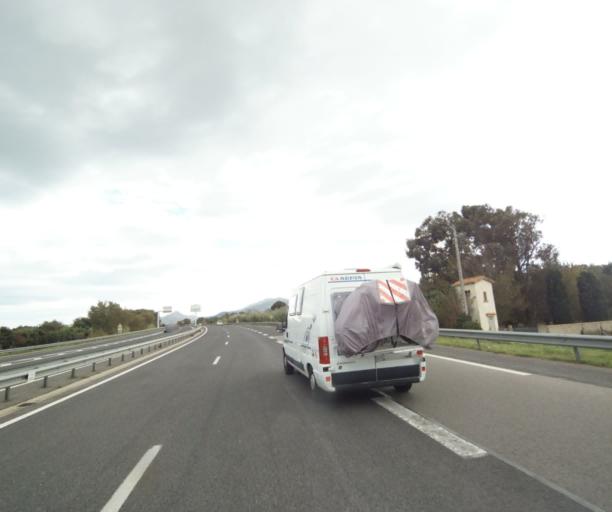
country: FR
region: Languedoc-Roussillon
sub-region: Departement des Pyrenees-Orientales
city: Elne
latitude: 42.5880
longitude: 2.9829
